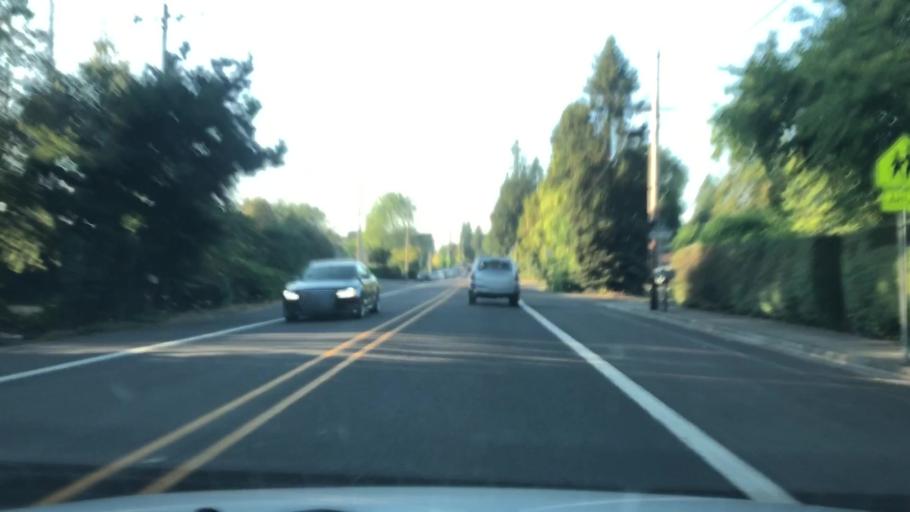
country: US
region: Oregon
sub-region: Clackamas County
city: Oak Grove
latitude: 45.4232
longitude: -122.6455
